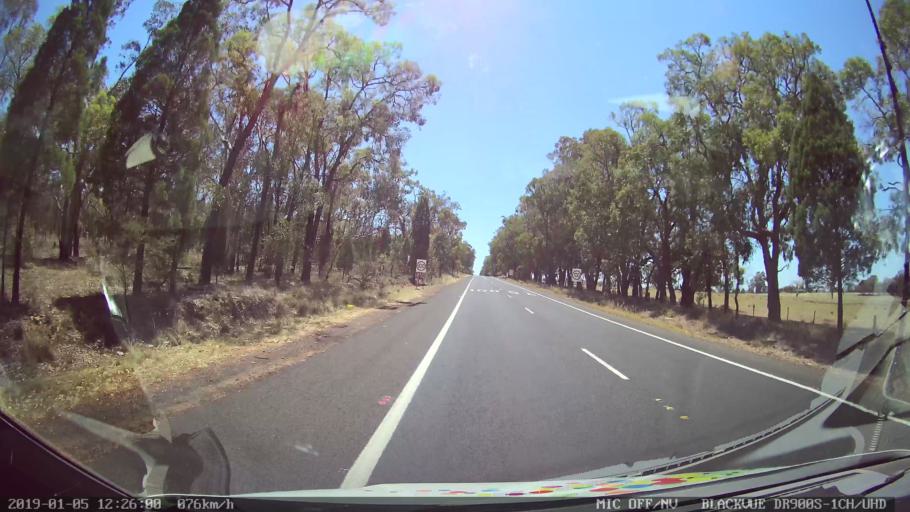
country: AU
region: New South Wales
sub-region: Warrumbungle Shire
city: Coonabarabran
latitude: -31.2569
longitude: 149.2907
